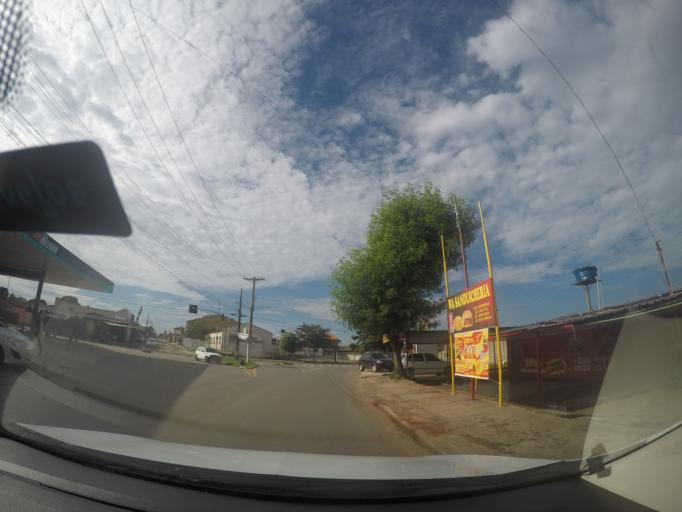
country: BR
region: Goias
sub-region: Goiania
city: Goiania
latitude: -16.6943
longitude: -49.1903
